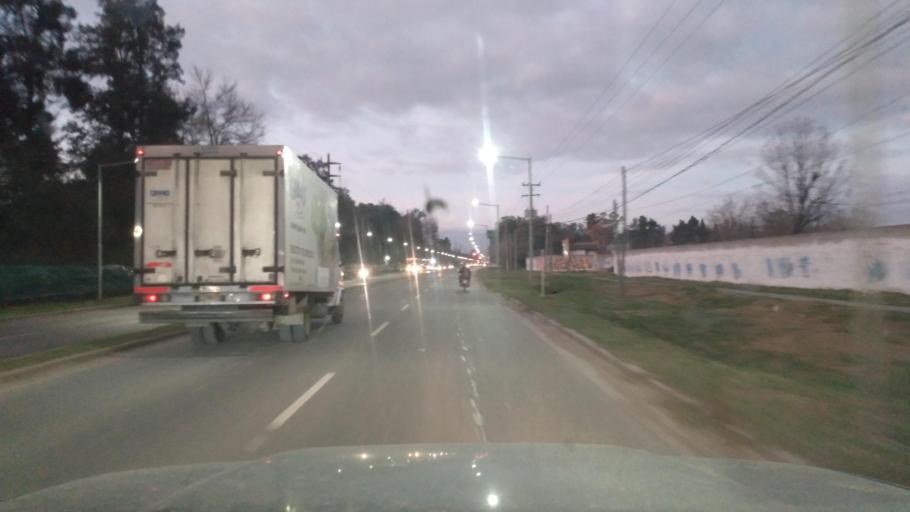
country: AR
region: Buenos Aires
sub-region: Partido de Pilar
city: Pilar
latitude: -34.4419
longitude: -58.8990
